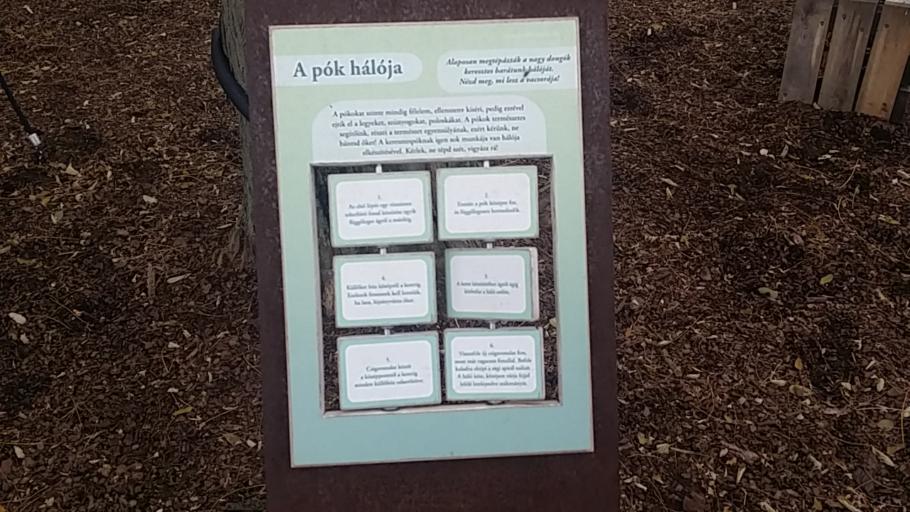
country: HU
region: Fejer
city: Szekesfehervar
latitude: 47.1648
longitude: 18.4152
